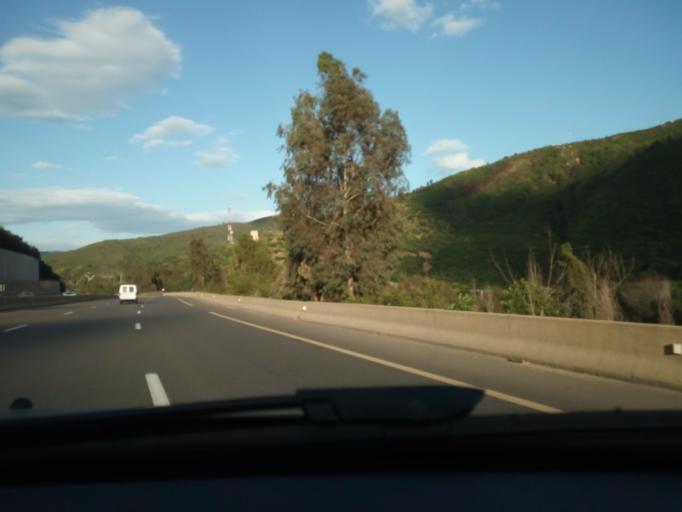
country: DZ
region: Tipaza
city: El Affroun
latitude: 36.3939
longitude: 2.5267
